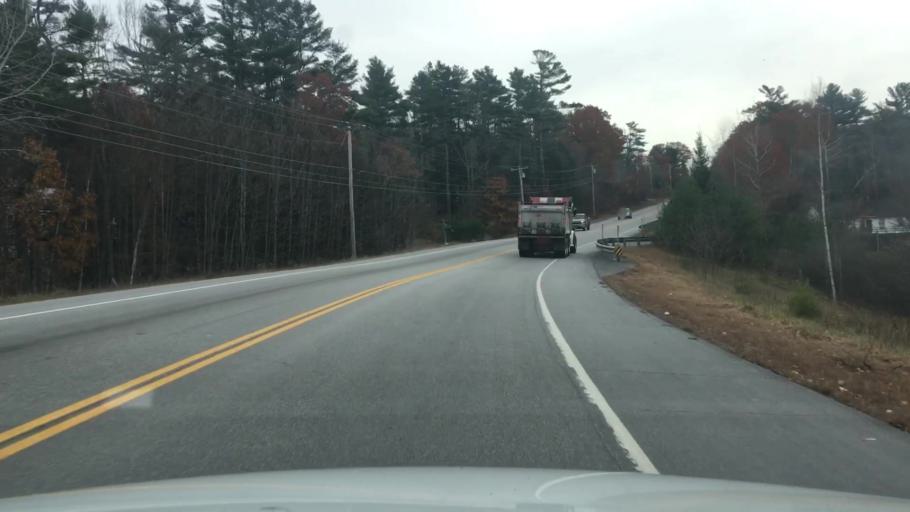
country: US
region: Maine
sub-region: Hancock County
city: Orland
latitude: 44.5575
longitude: -68.6988
